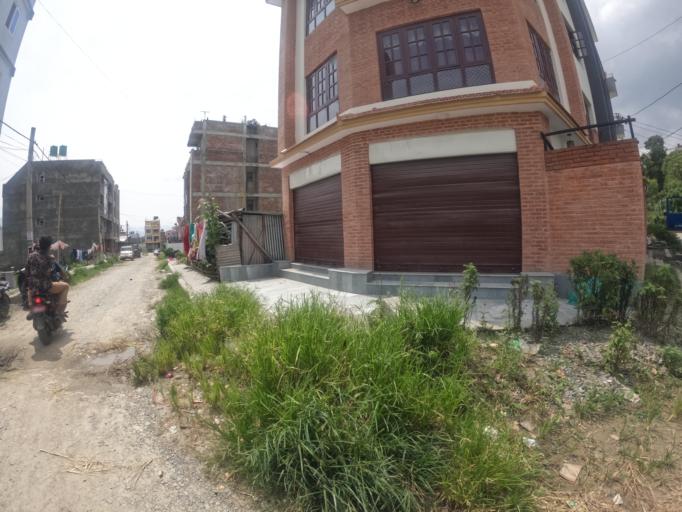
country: NP
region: Central Region
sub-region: Bagmati Zone
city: Bhaktapur
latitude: 27.6779
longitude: 85.3889
